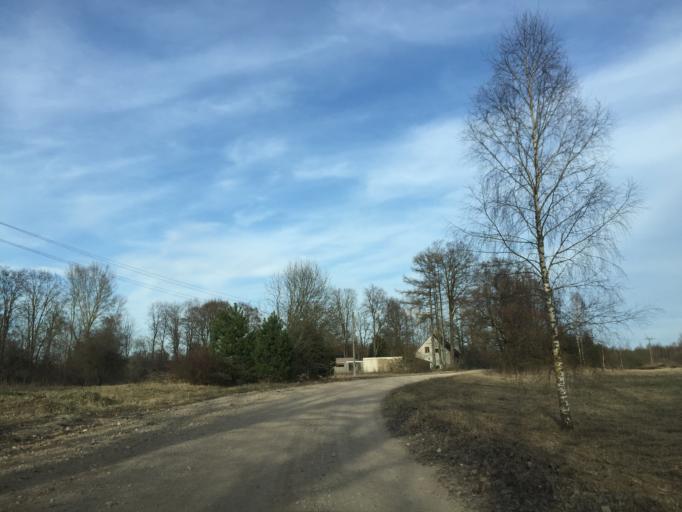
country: LV
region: Kegums
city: Kegums
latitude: 56.8069
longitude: 24.7796
